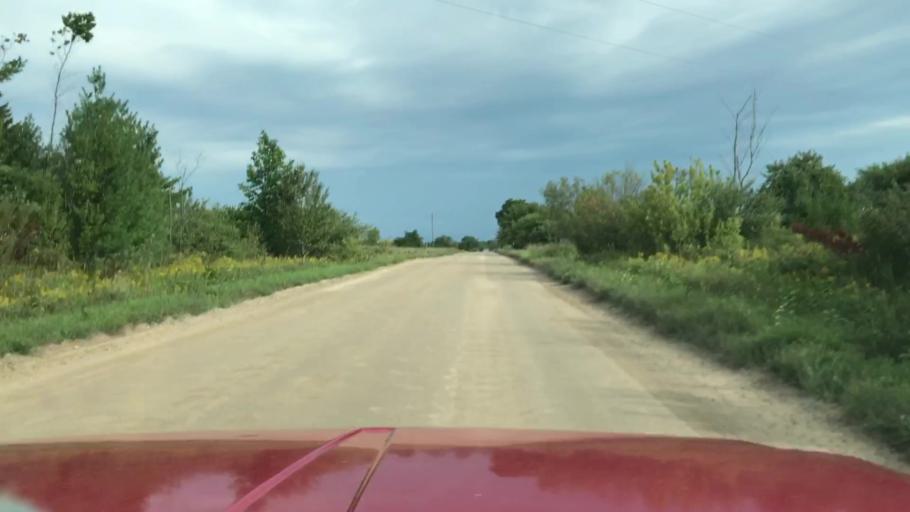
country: US
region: Michigan
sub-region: Charlevoix County
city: Charlevoix
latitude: 45.7240
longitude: -85.5158
